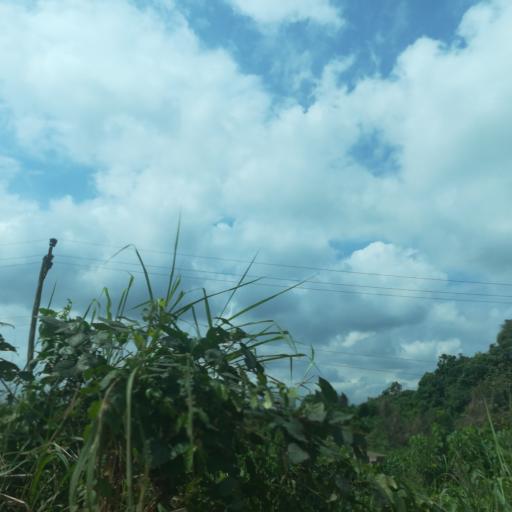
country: NG
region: Ogun
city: Odogbolu
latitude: 6.6518
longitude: 3.7031
